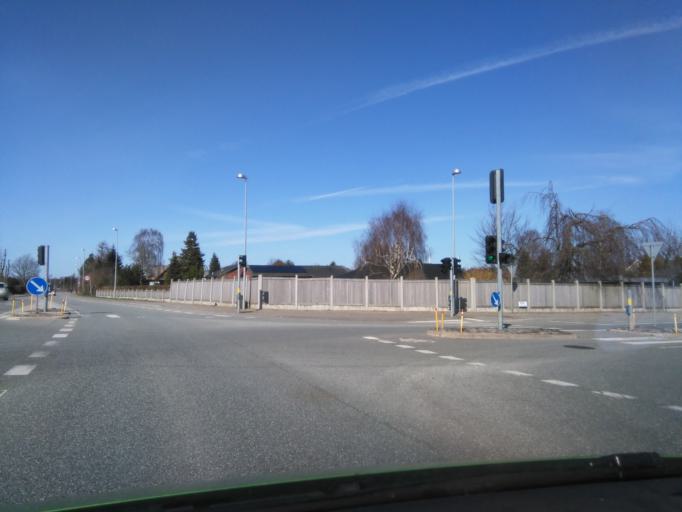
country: DK
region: Central Jutland
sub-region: Favrskov Kommune
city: Hinnerup
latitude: 56.2534
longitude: 10.0683
